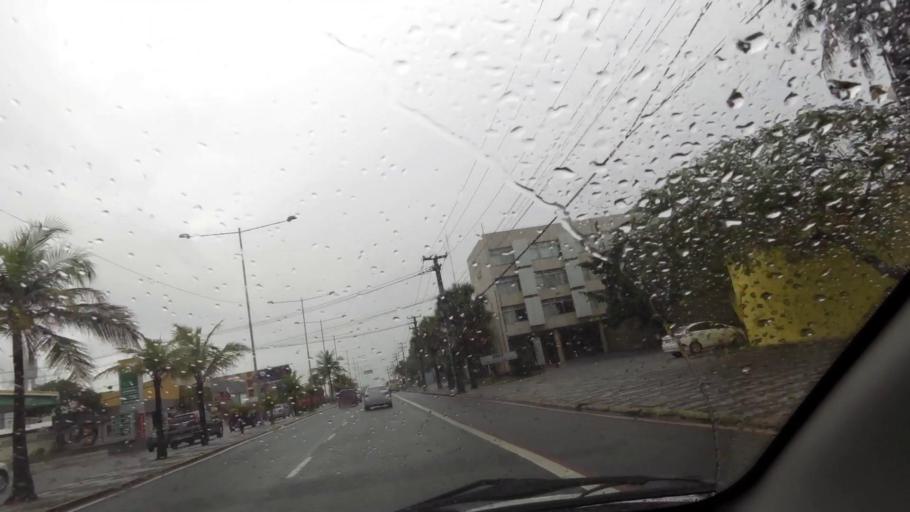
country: BR
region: Pernambuco
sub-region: Recife
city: Recife
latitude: -8.0853
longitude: -34.8867
